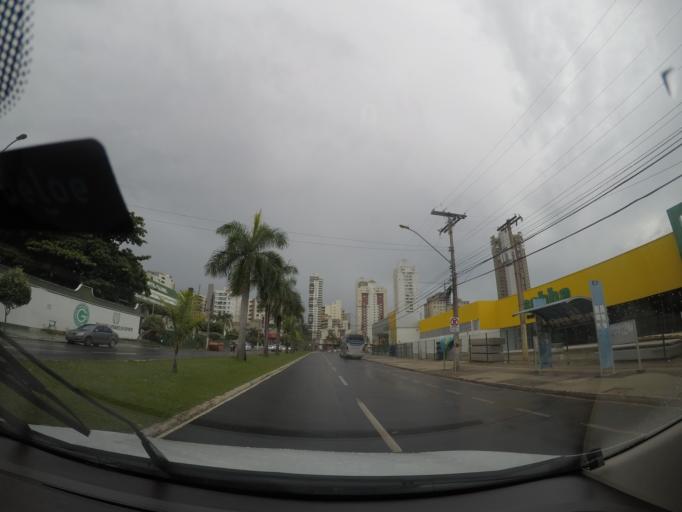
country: BR
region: Goias
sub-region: Goiania
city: Goiania
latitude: -16.7100
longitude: -49.2627
